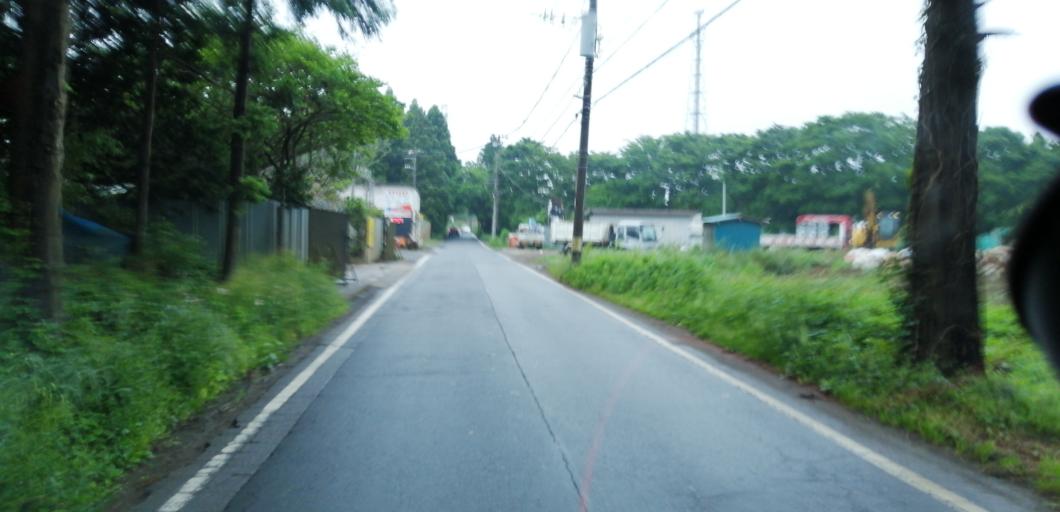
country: JP
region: Chiba
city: Oami
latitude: 35.5650
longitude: 140.2566
